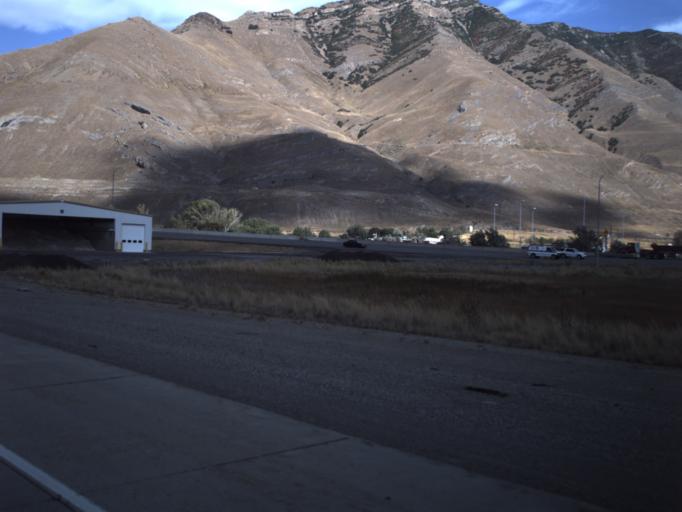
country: US
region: Utah
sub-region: Tooele County
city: Stansbury park
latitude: 40.6917
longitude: -112.2652
